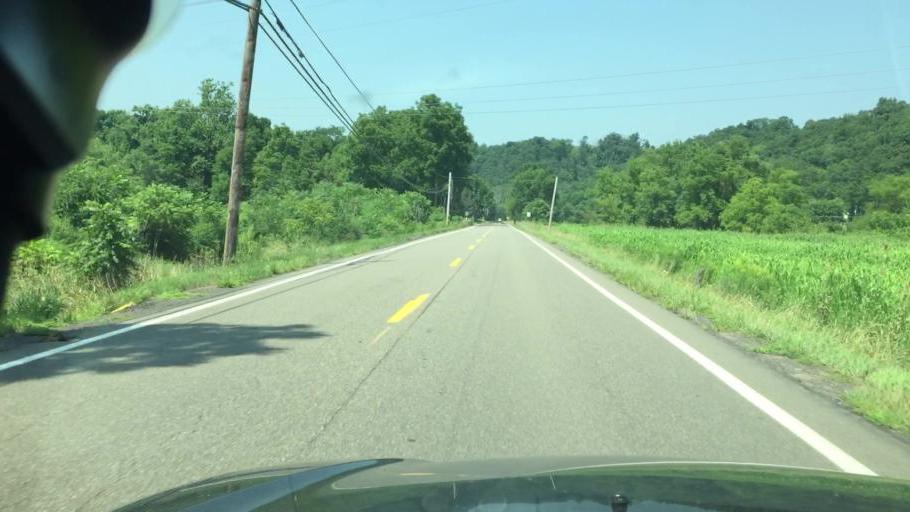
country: US
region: Pennsylvania
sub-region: Columbia County
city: Almedia
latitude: 40.9800
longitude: -76.3804
